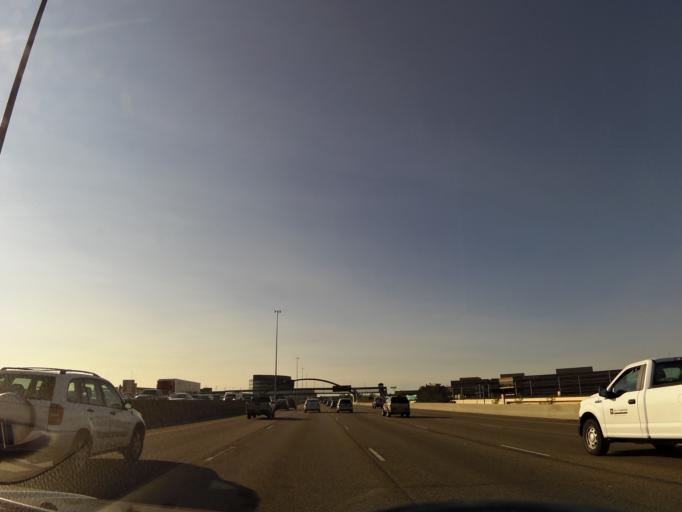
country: US
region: Colorado
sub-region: Arapahoe County
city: Centennial
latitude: 39.5820
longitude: -104.8777
